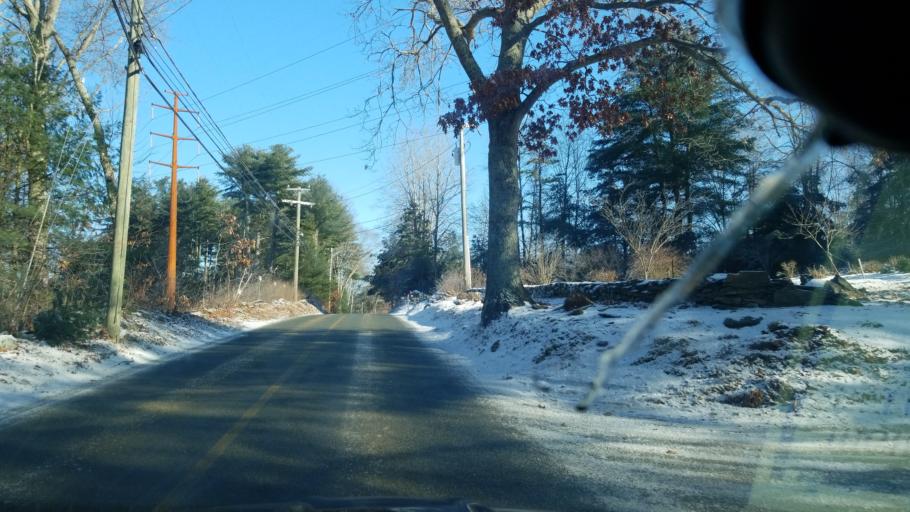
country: US
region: Connecticut
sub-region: Windham County
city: East Brooklyn
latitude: 41.7904
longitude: -71.9169
